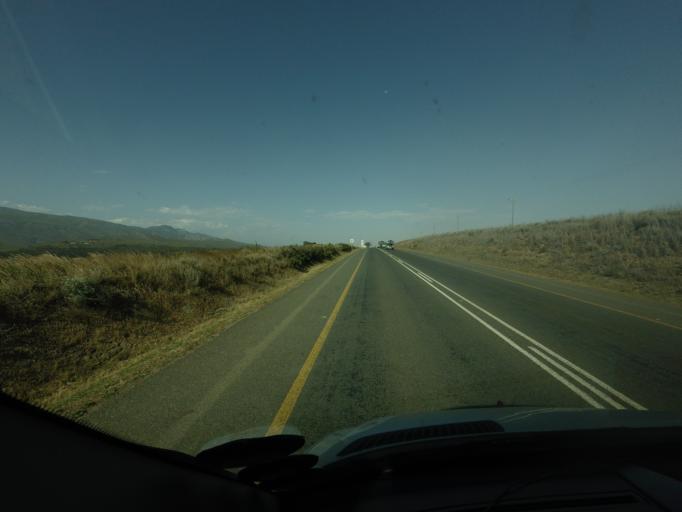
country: ZA
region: Western Cape
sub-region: Cape Winelands District Municipality
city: Ashton
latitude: -34.1520
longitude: 19.9032
